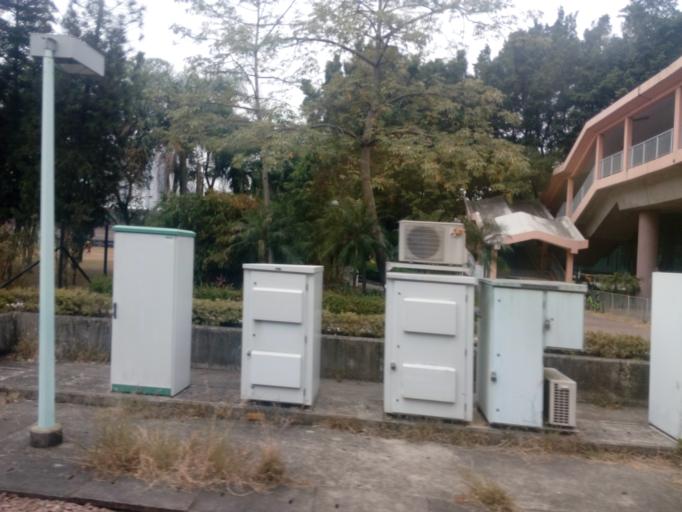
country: HK
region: Yuen Long
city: Yuen Long Kau Hui
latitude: 22.4553
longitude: 114.0059
